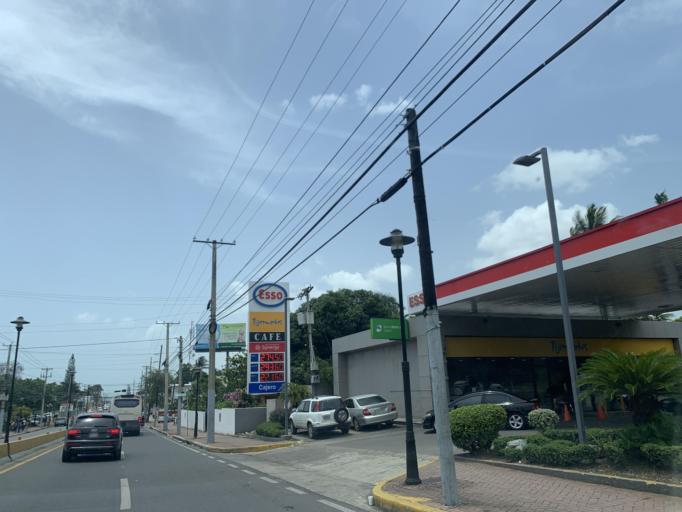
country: DO
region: Puerto Plata
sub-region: Puerto Plata
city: Puerto Plata
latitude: 19.7855
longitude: -70.6863
